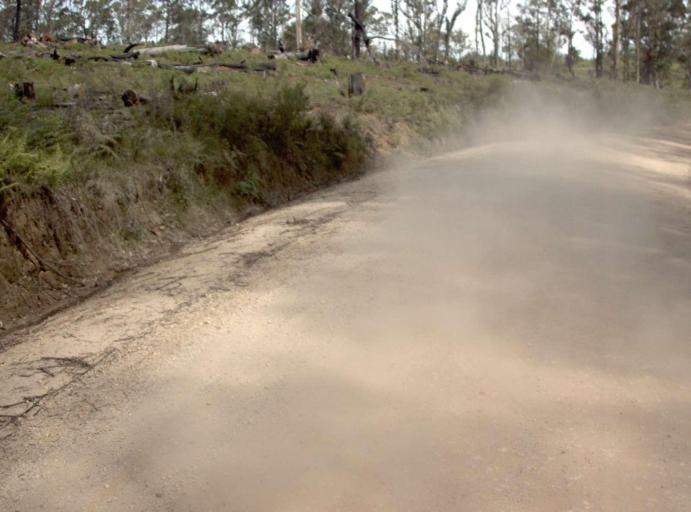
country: AU
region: Victoria
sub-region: East Gippsland
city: Lakes Entrance
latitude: -37.6255
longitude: 148.6782
